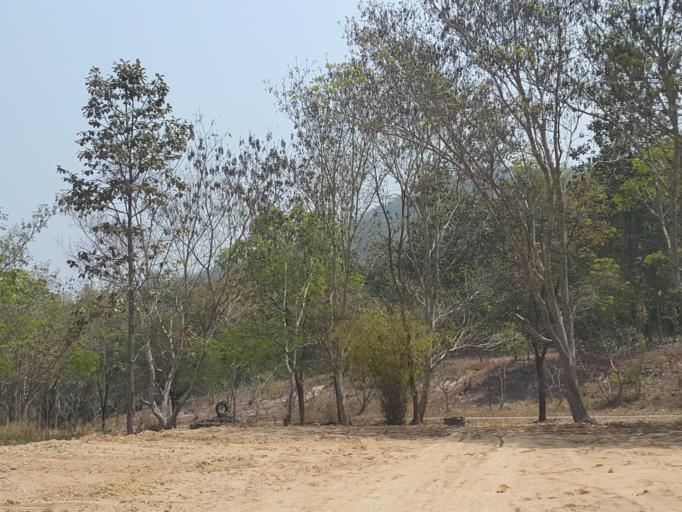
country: TH
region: Chiang Mai
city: Mae On
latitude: 18.7008
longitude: 99.2064
